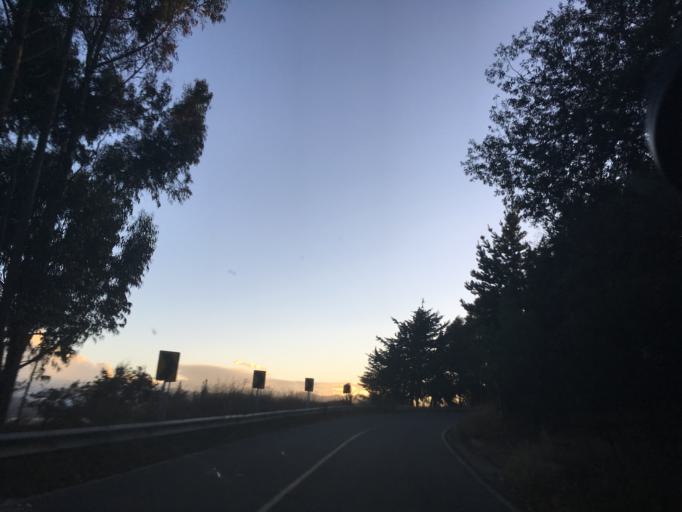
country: CO
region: Boyaca
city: Aquitania
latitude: 5.5694
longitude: -72.8898
